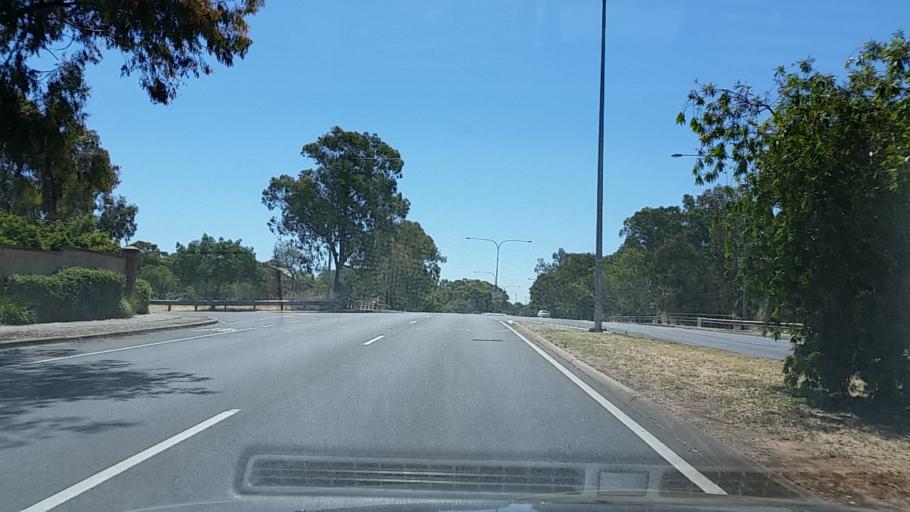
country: AU
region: South Australia
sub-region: Norwood Payneham St Peters
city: Marden
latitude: -34.8912
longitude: 138.6320
